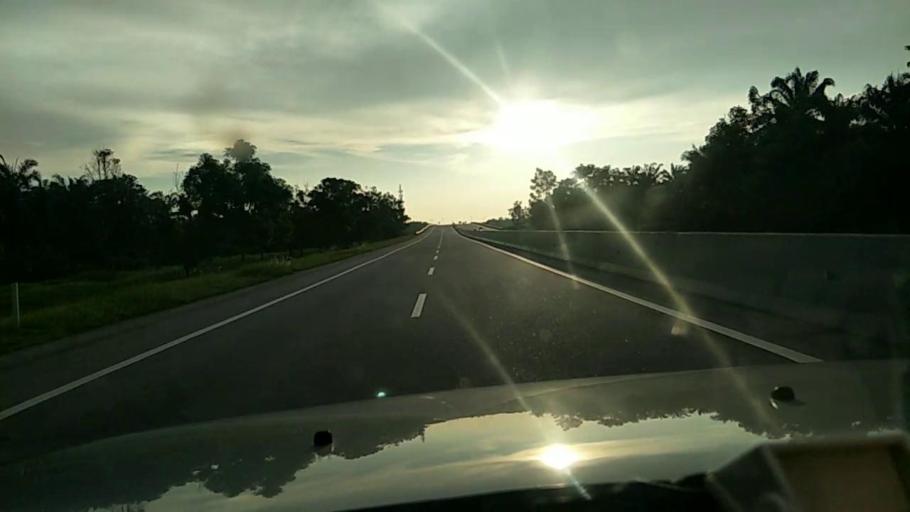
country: MY
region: Selangor
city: Batu Arang
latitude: 3.2885
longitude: 101.4101
